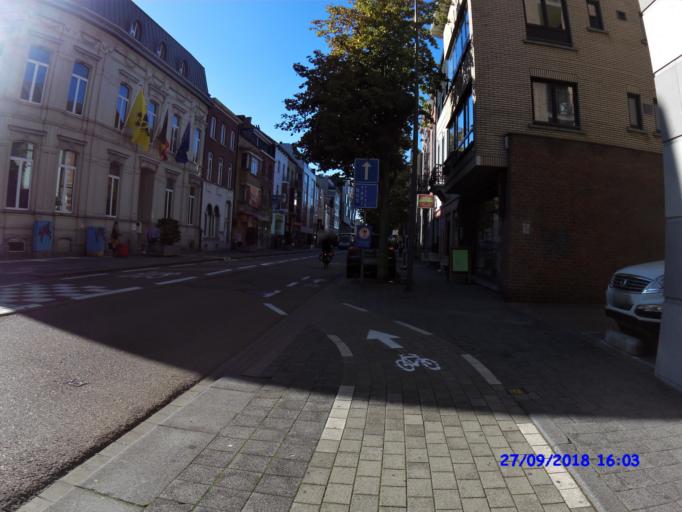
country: BE
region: Flanders
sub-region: Provincie Limburg
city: Hasselt
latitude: 50.9300
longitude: 5.3321
